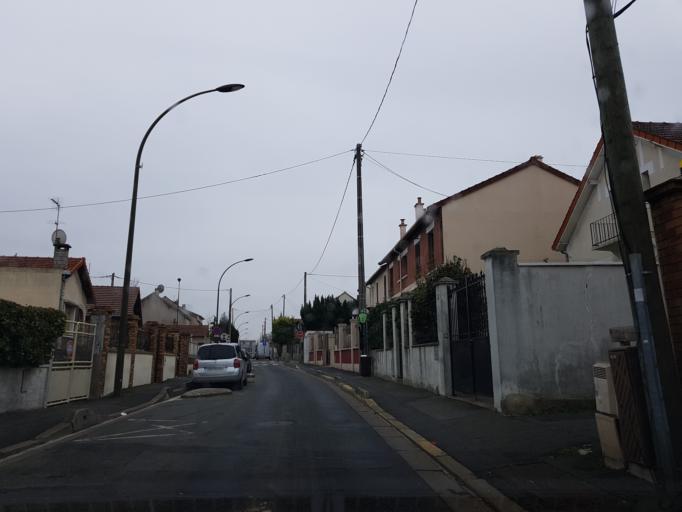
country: FR
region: Ile-de-France
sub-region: Departement du Val-de-Marne
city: Villejuif
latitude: 48.7993
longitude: 2.3698
